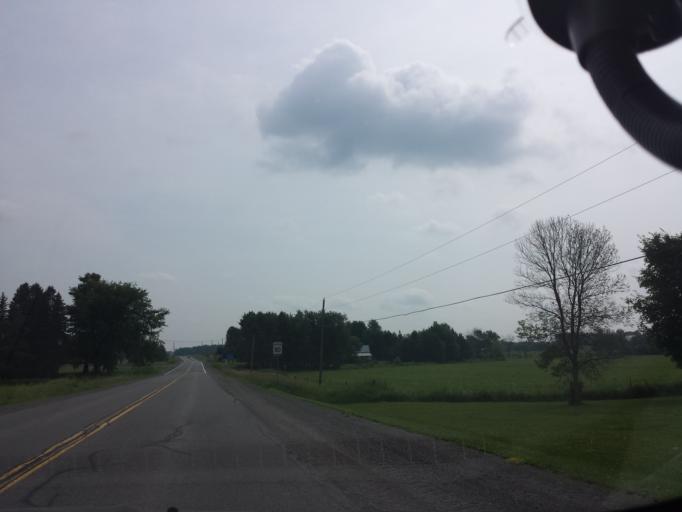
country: CA
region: Ontario
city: Clarence-Rockland
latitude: 45.3843
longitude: -75.3365
